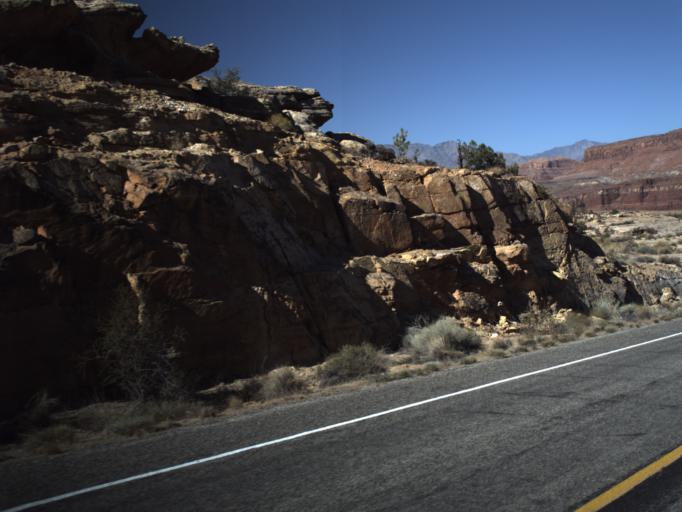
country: US
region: Utah
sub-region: San Juan County
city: Blanding
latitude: 37.8822
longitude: -110.3582
